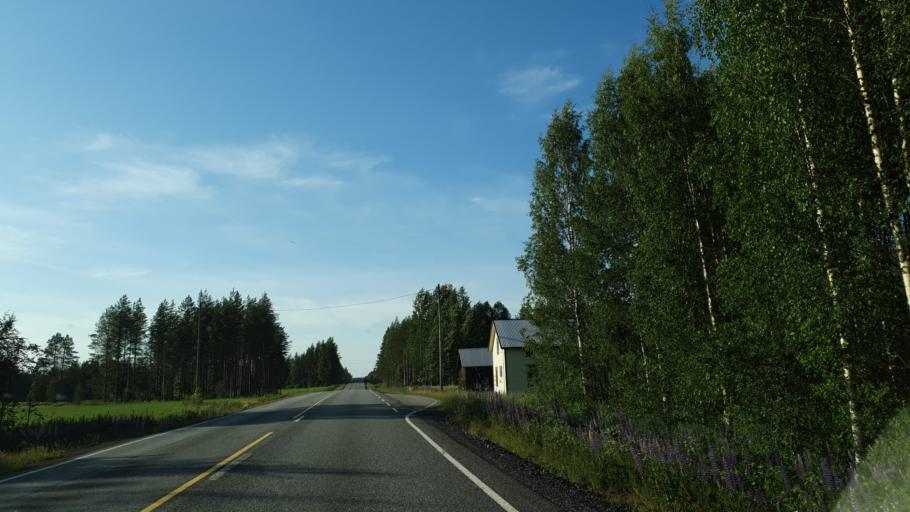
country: FI
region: Kainuu
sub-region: Kehys-Kainuu
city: Kuhmo
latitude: 64.0804
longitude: 29.4859
